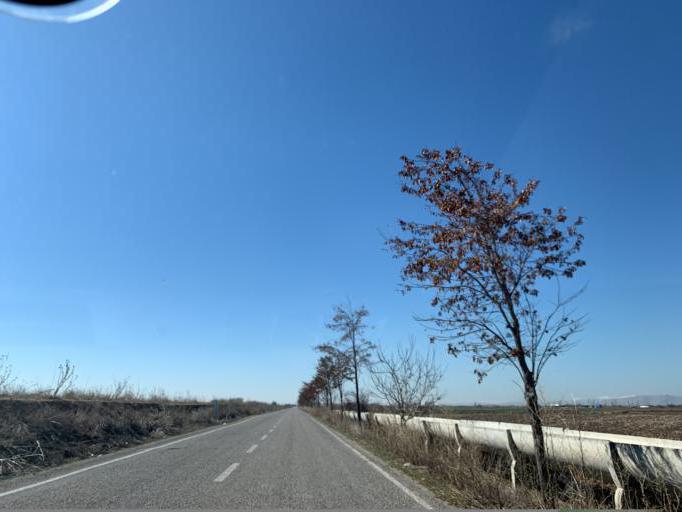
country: TR
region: Konya
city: Catalhoeyuek
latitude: 37.6229
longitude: 32.8035
